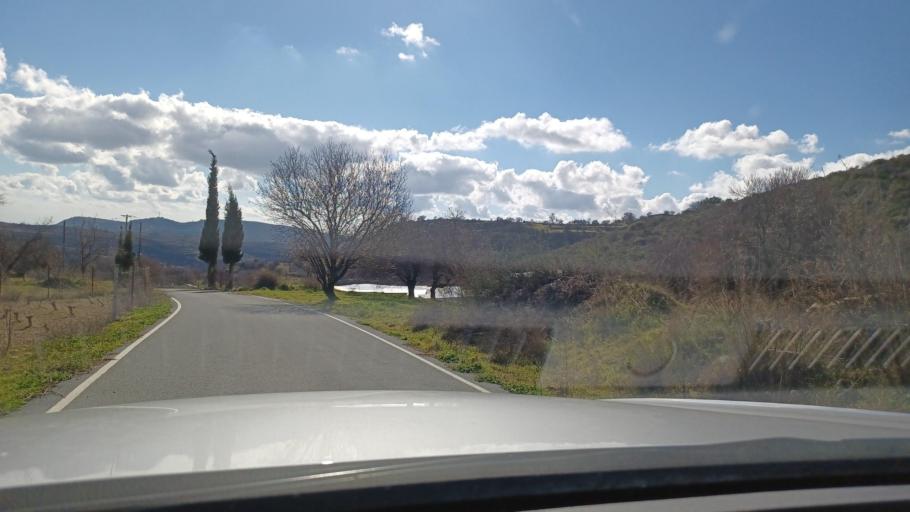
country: CY
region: Limassol
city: Pachna
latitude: 34.8284
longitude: 32.8066
